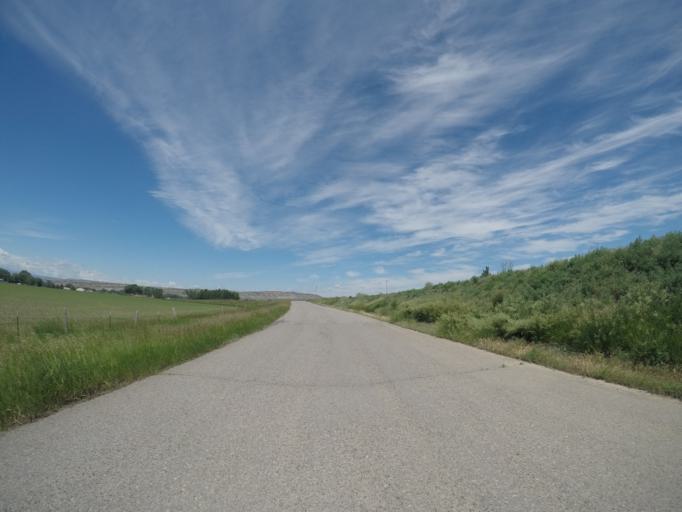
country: US
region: Montana
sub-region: Carbon County
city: Red Lodge
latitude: 45.2565
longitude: -108.8871
